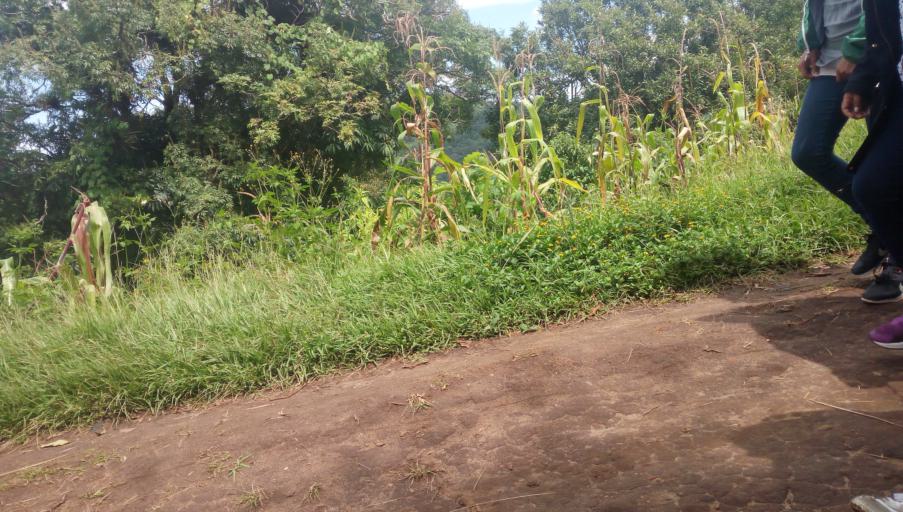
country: GT
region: Guatemala
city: Santa Catarina Pinula
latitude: 14.5317
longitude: -90.4956
